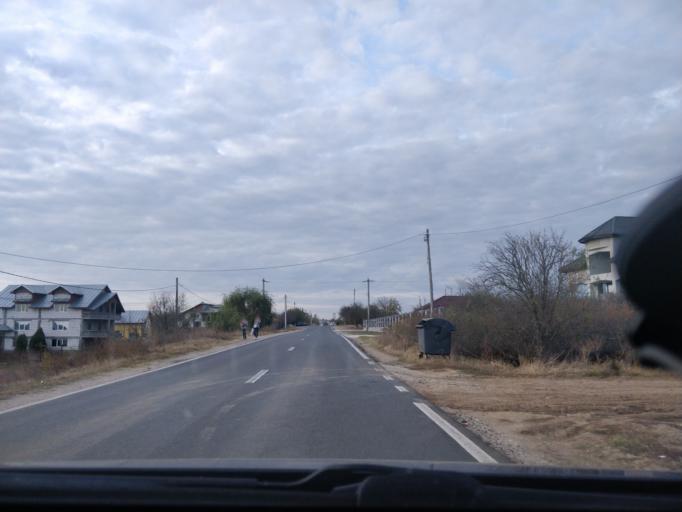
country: RO
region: Giurgiu
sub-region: Comuna Crevedia Mare
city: Dealu
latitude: 44.4118
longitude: 25.6411
